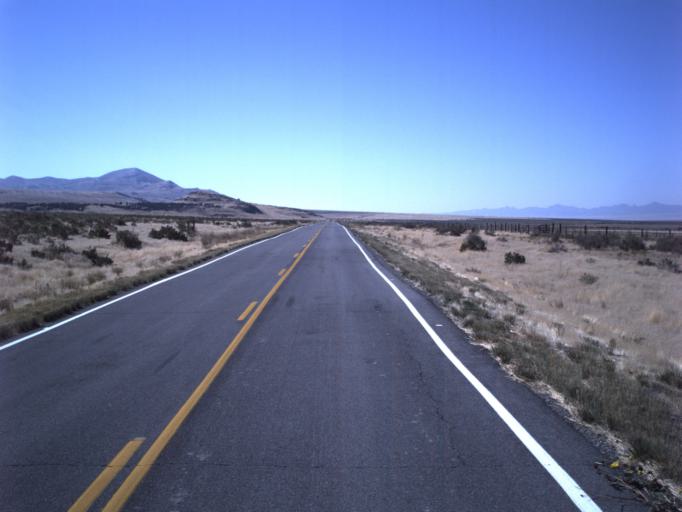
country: US
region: Utah
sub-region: Tooele County
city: Grantsville
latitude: 40.6307
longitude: -112.6952
